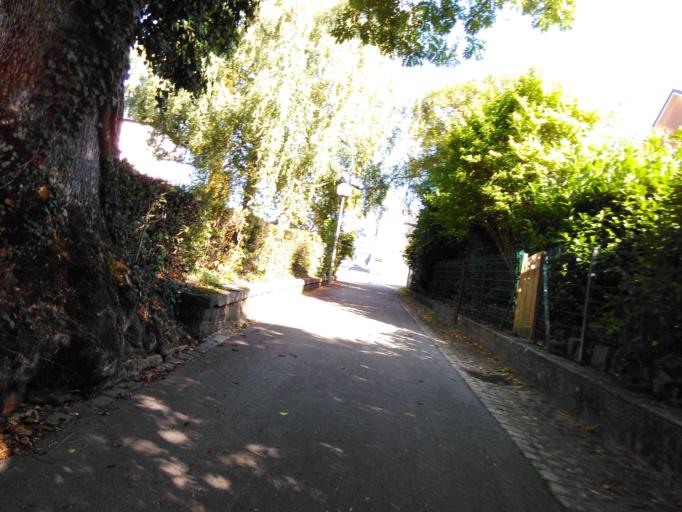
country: LU
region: Luxembourg
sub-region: Canton de Capellen
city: Steinfort
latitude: 49.6471
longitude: 5.9167
